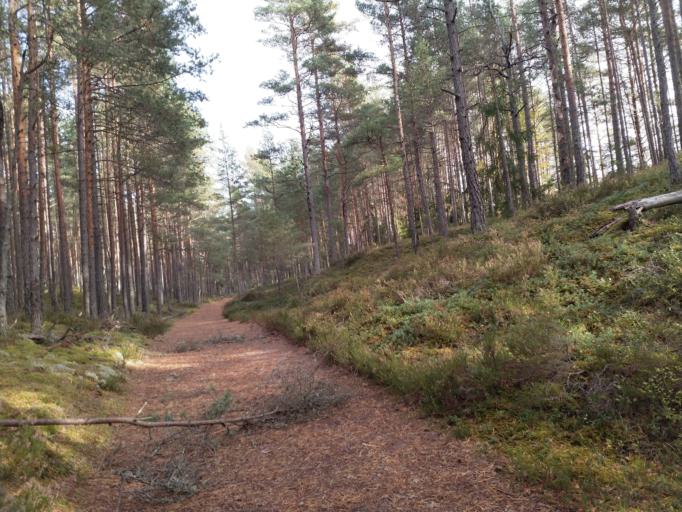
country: LV
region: Dundaga
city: Dundaga
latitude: 57.6529
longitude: 22.2638
